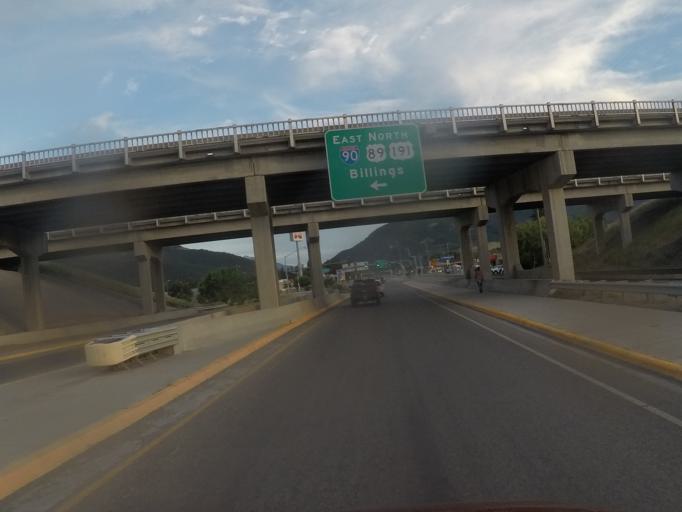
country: US
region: Montana
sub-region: Park County
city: Livingston
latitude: 45.6449
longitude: -110.5736
